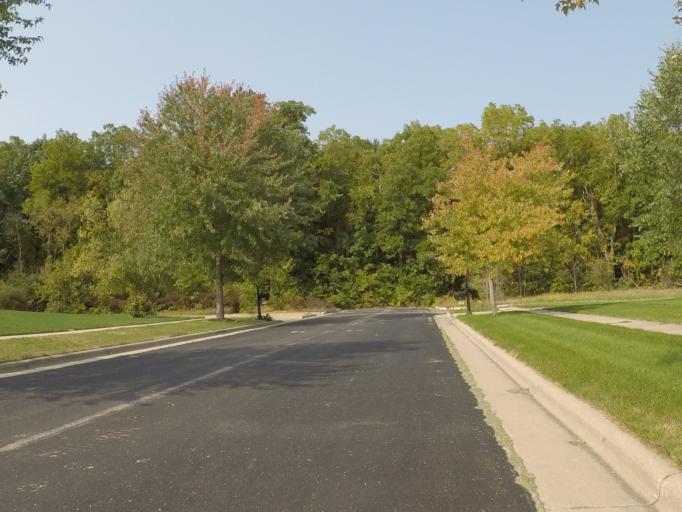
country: US
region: Wisconsin
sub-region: Dane County
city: Verona
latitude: 43.0368
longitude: -89.5372
